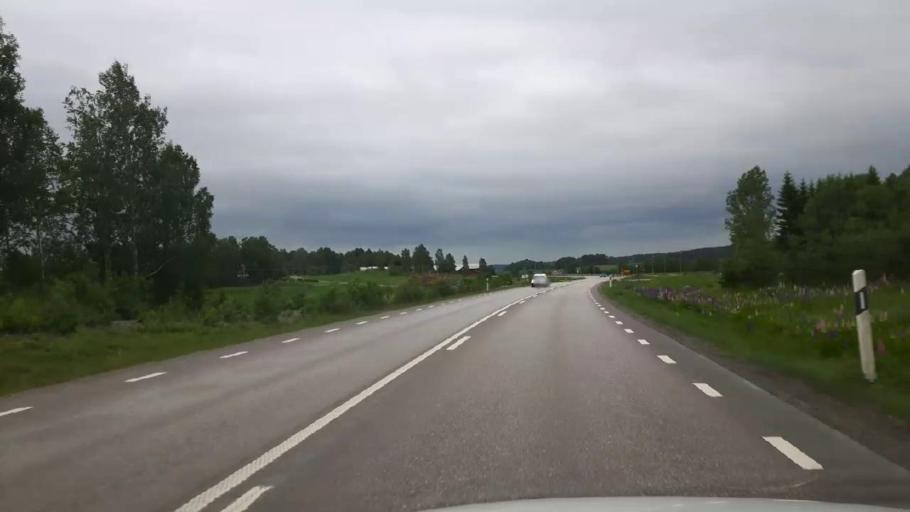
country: SE
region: Vaestmanland
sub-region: Kopings Kommun
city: Kolsva
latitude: 59.5742
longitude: 15.8791
